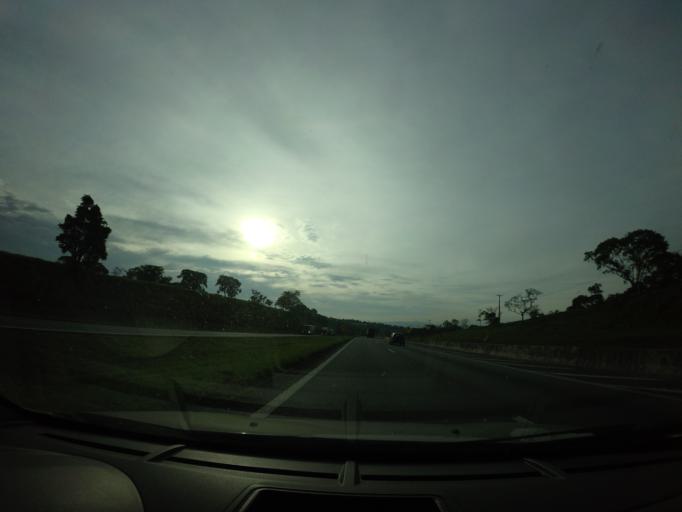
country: BR
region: Sao Paulo
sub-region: Jarinu
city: Jarinu
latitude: -23.0634
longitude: -46.6490
